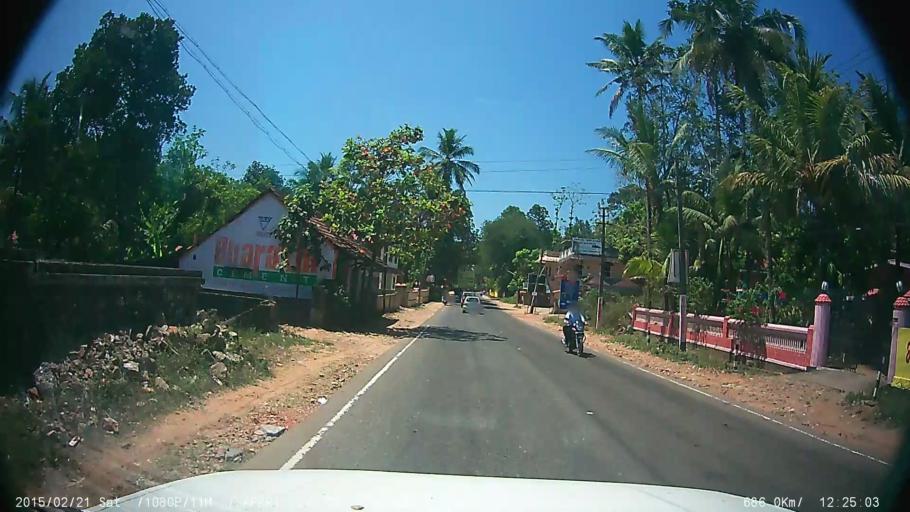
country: IN
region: Kerala
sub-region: Kottayam
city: Palackattumala
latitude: 9.6690
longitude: 76.5776
